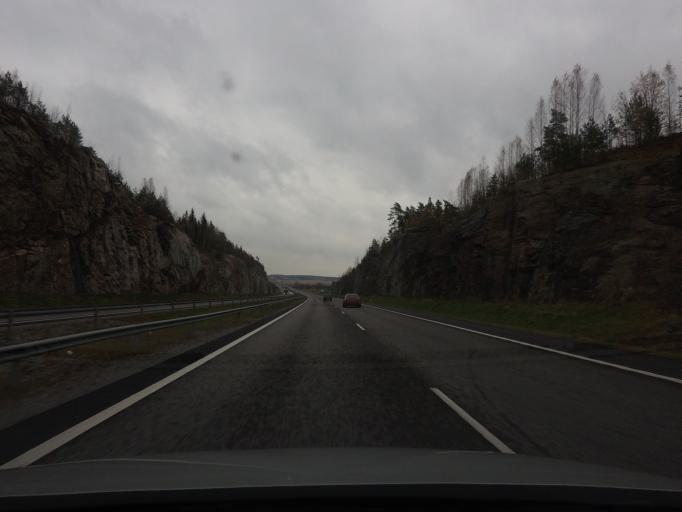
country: FI
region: Varsinais-Suomi
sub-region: Salo
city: Halikko
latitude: 60.4318
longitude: 22.9943
